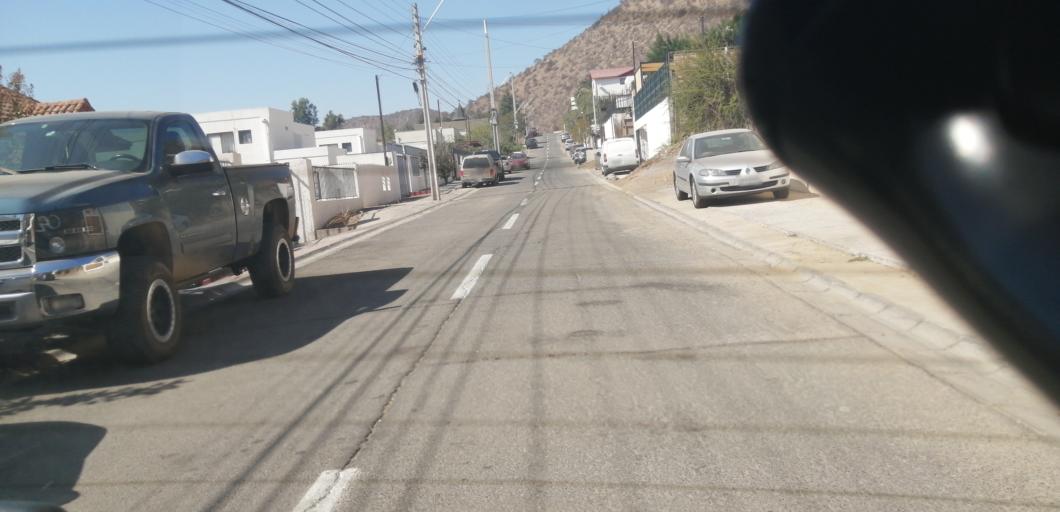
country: CL
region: Santiago Metropolitan
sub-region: Provincia de Santiago
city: Lo Prado
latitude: -33.4575
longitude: -70.8242
